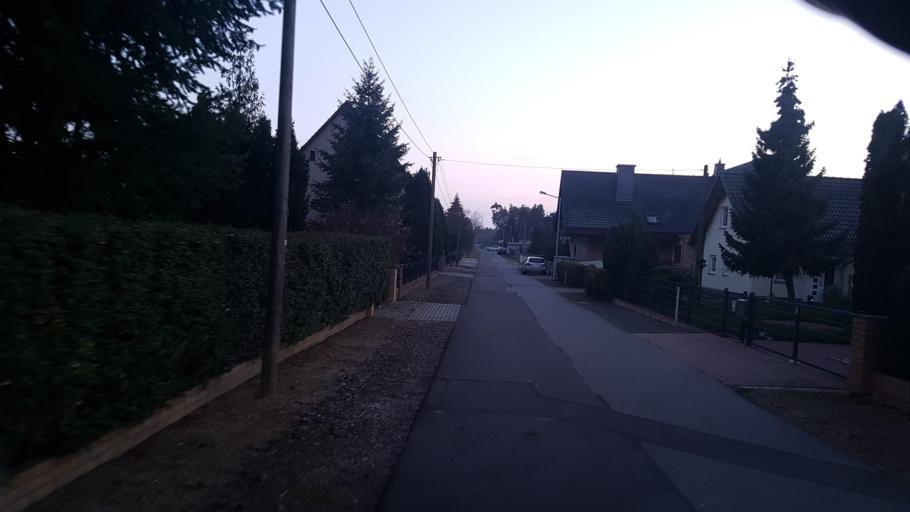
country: DE
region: Brandenburg
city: Lauchhammer
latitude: 51.5140
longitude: 13.7168
